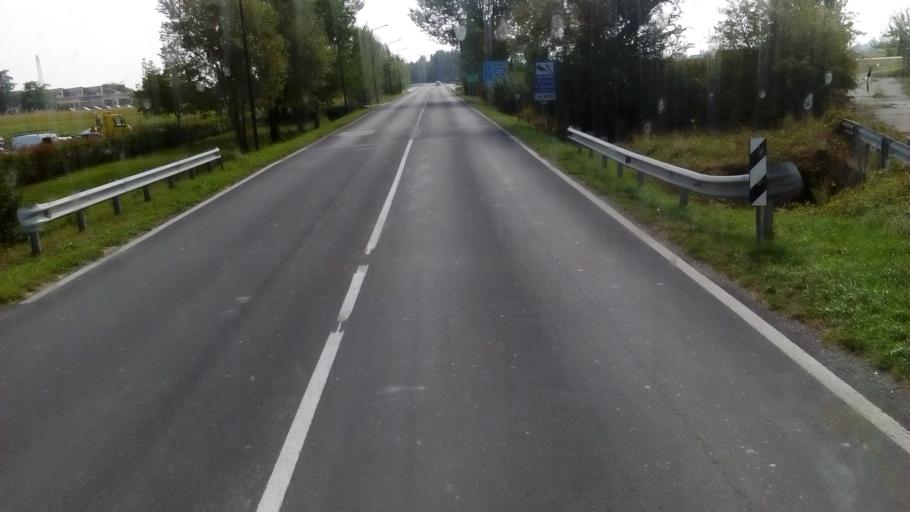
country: IT
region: Veneto
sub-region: Provincia di Rovigo
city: Castelnovo Bariano
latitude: 45.0399
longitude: 11.2916
